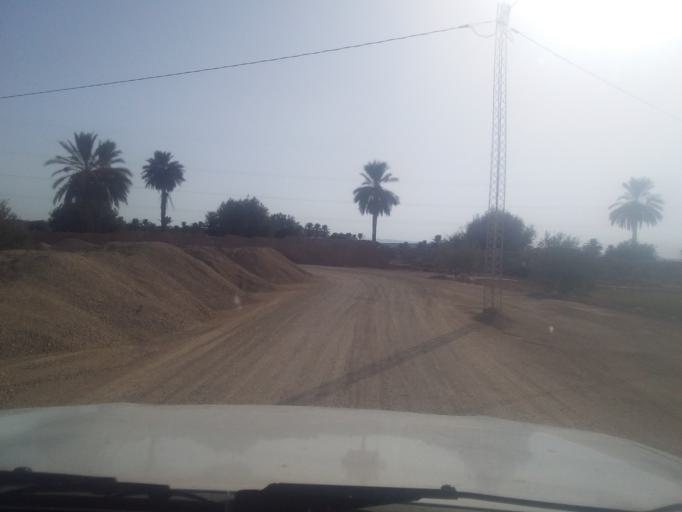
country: TN
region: Qabis
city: Matmata
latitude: 33.5899
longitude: 10.2676
